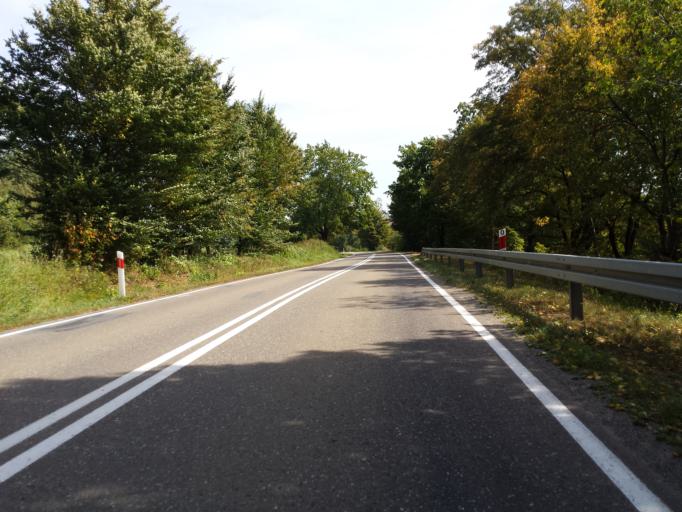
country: PL
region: Subcarpathian Voivodeship
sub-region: Powiat leski
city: Lesko
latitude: 49.4145
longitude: 22.3075
